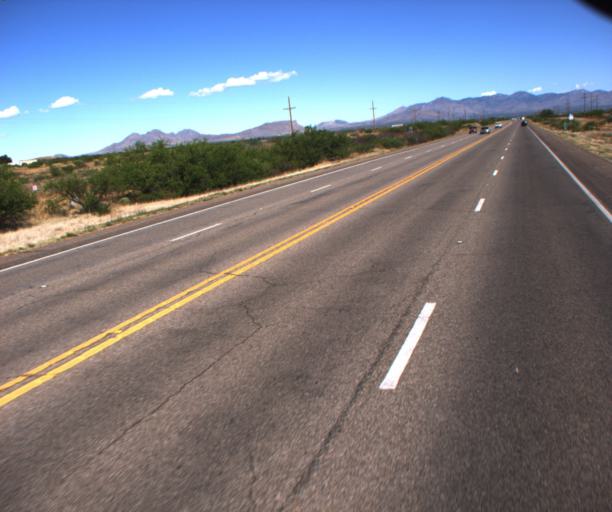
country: US
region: Arizona
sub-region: Cochise County
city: Sierra Vista
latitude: 31.5891
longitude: -110.3222
